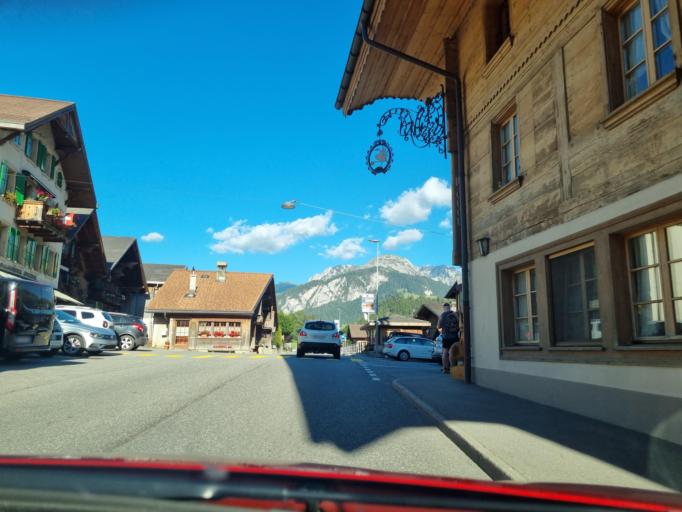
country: CH
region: Vaud
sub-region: Riviera-Pays-d'Enhaut District
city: Chateau-d'Oex
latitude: 46.4674
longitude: 7.0815
